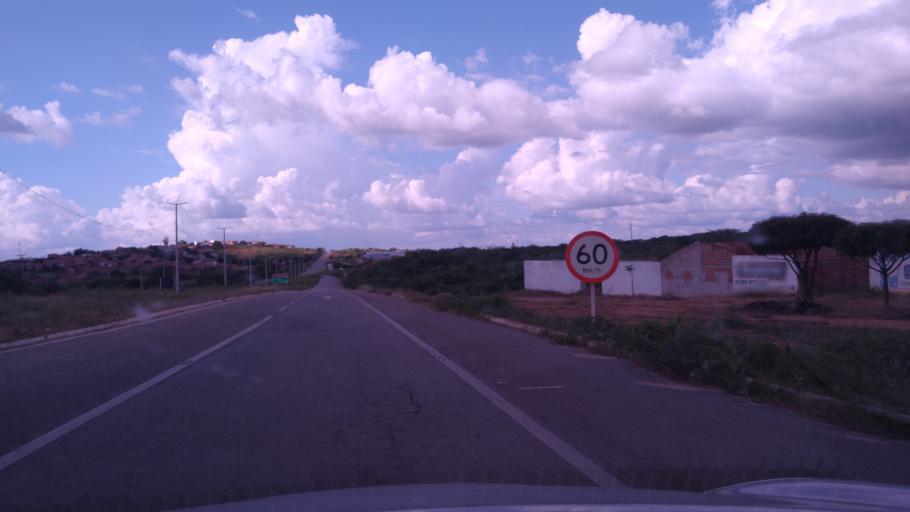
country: BR
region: Ceara
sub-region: Caninde
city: Caninde
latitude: -4.3793
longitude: -39.3092
